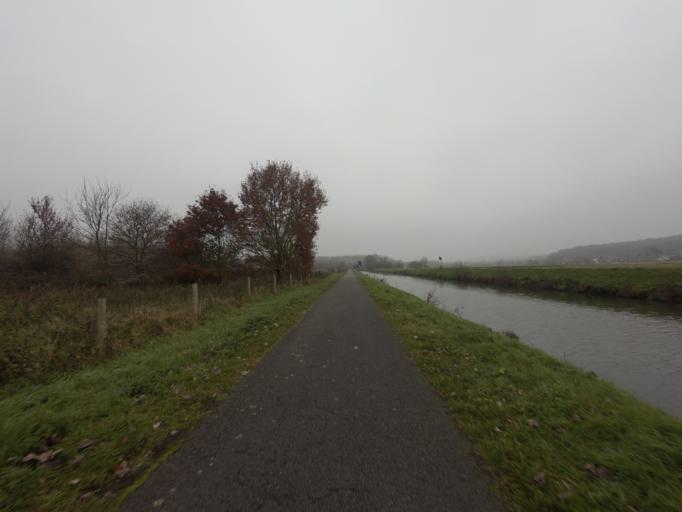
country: BE
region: Flanders
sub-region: Provincie Oost-Vlaanderen
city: Geraardsbergen
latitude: 50.7517
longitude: 3.8588
